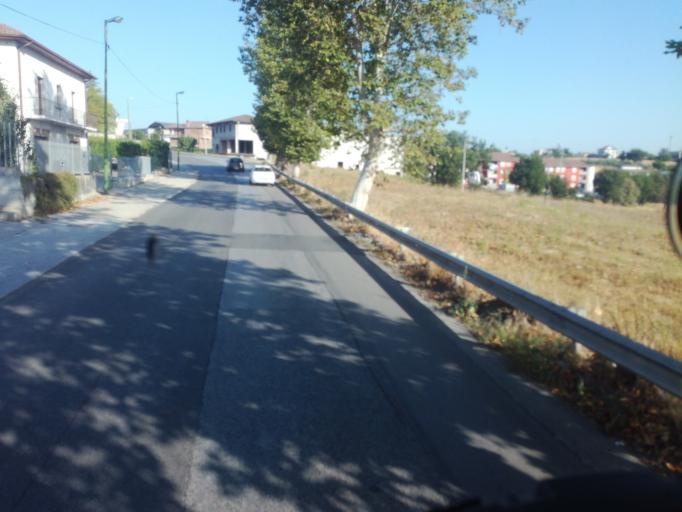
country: IT
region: Campania
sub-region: Provincia di Avellino
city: Grottaminarda
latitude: 41.0700
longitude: 15.0712
